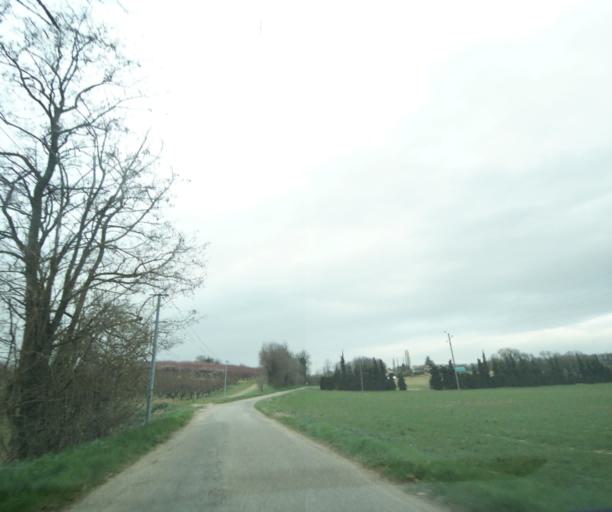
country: FR
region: Rhone-Alpes
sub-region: Departement de la Drome
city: Bourg-les-Valence
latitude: 44.9710
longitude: 4.9150
